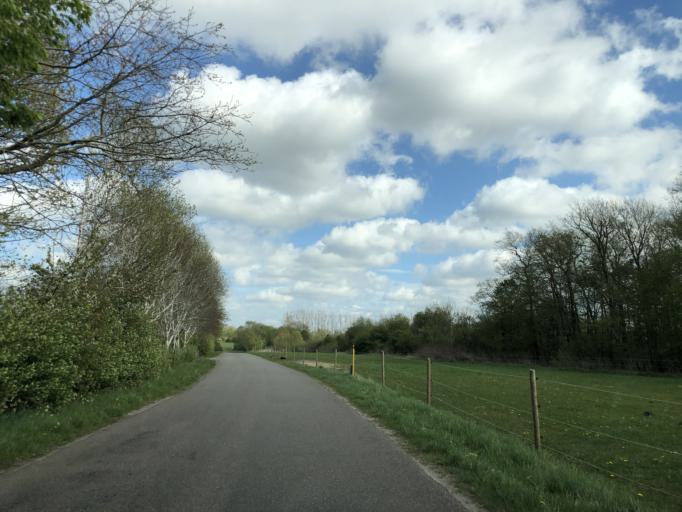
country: DK
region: Central Jutland
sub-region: Herning Kommune
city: Avlum
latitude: 56.3047
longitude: 8.7594
